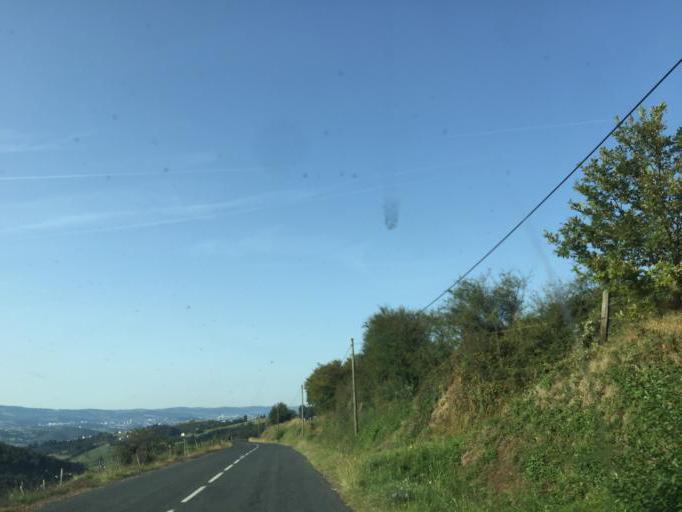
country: FR
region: Rhone-Alpes
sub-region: Departement de la Loire
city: Sorbiers
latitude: 45.5179
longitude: 4.4603
